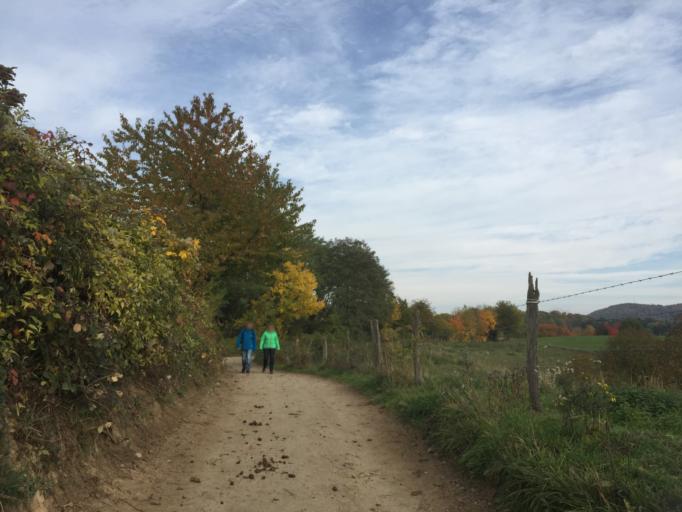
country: DE
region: Hesse
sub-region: Regierungsbezirk Darmstadt
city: Bensheim
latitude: 49.6843
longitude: 8.6507
